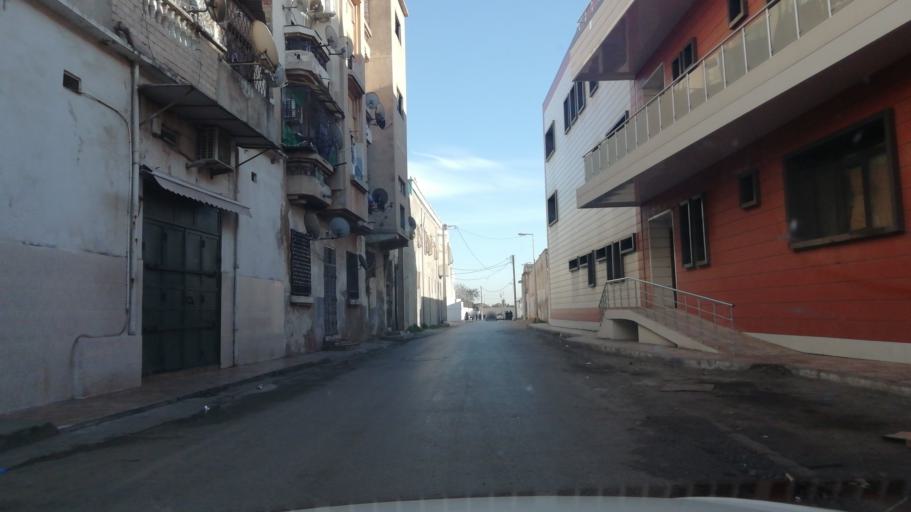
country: DZ
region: Oran
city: Oran
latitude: 35.6948
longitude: -0.6391
